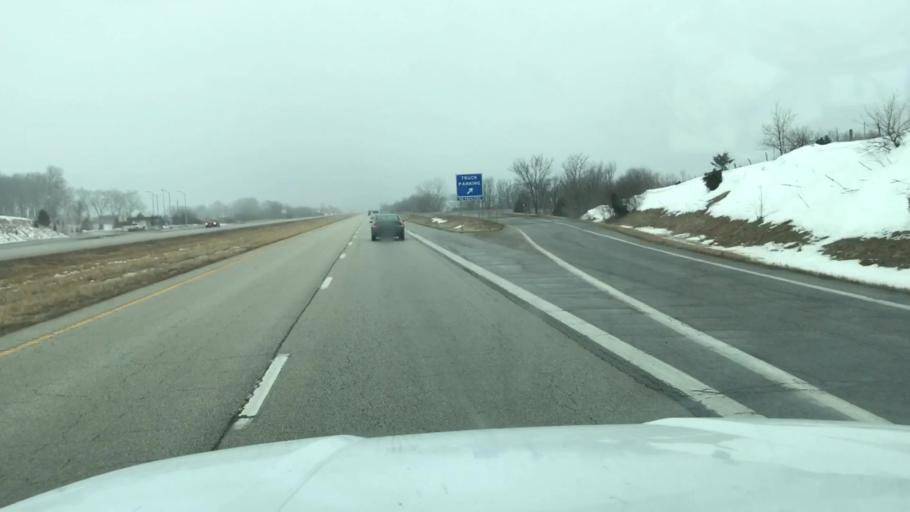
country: US
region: Missouri
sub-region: Andrew County
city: Country Club Village
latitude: 39.7478
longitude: -94.6929
